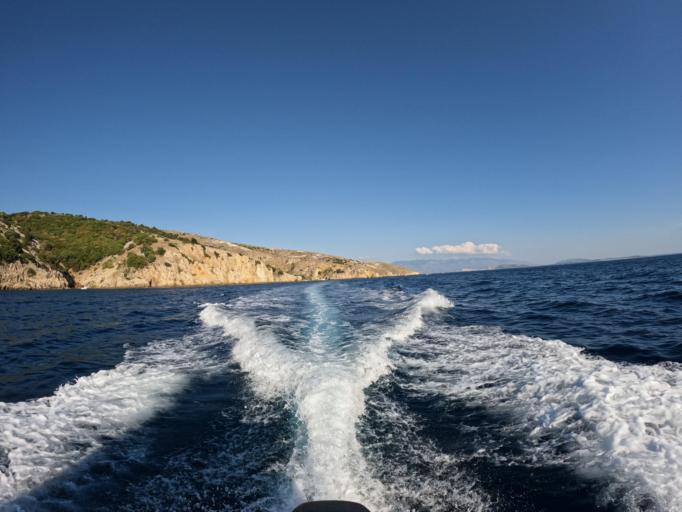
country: HR
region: Primorsko-Goranska
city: Punat
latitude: 44.9737
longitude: 14.6284
